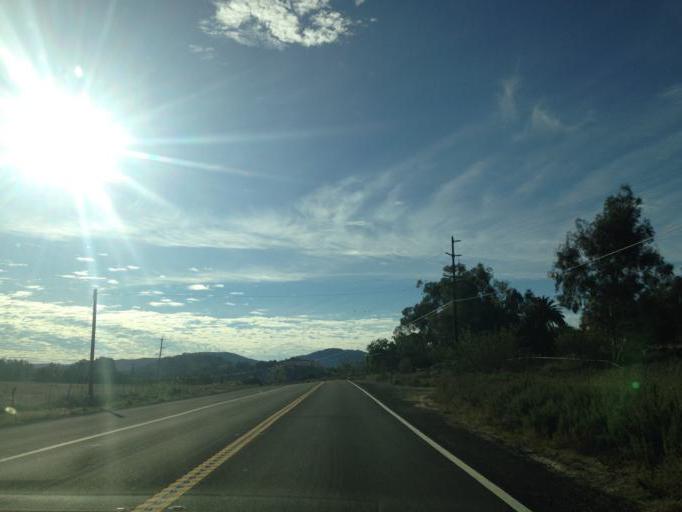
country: US
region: California
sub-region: San Diego County
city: Valley Center
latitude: 33.2965
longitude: -116.9071
